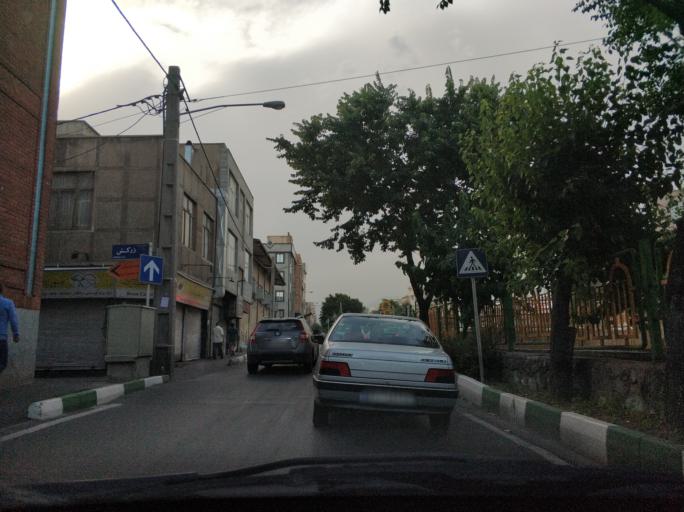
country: IR
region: Tehran
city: Tehran
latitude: 35.7152
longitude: 51.4820
